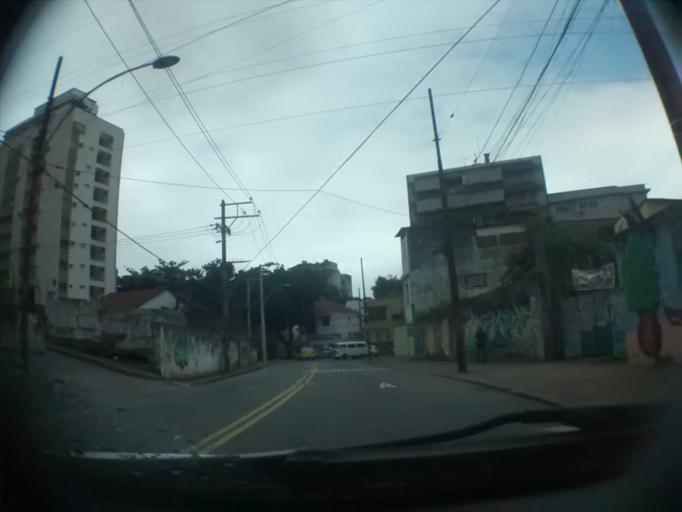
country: BR
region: Rio de Janeiro
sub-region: Rio De Janeiro
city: Rio de Janeiro
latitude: -22.9367
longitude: -43.2470
